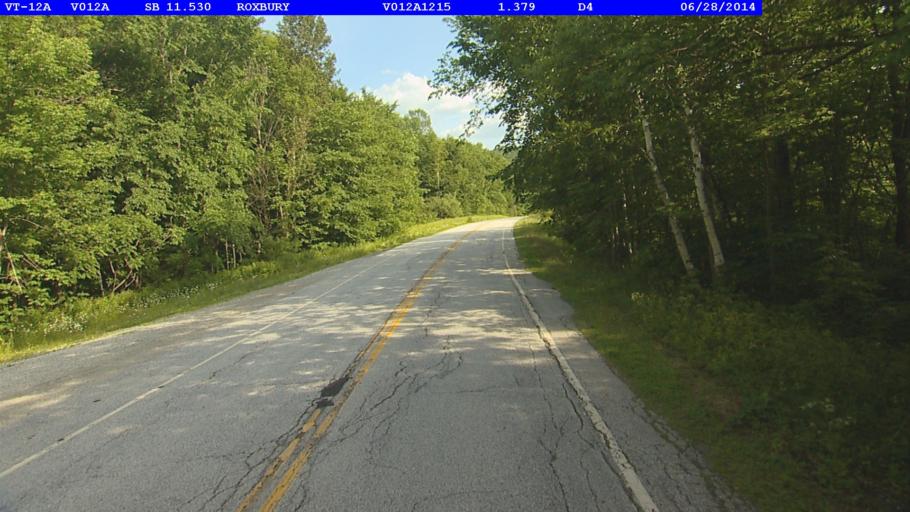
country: US
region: Vermont
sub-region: Washington County
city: Northfield
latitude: 44.0485
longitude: -72.7433
